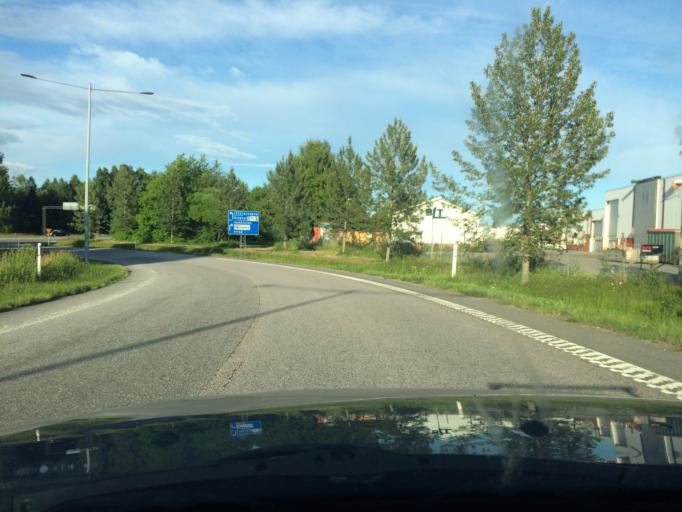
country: SE
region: Norrbotten
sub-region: Pitea Kommun
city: Bergsviken
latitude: 65.3197
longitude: 21.4254
